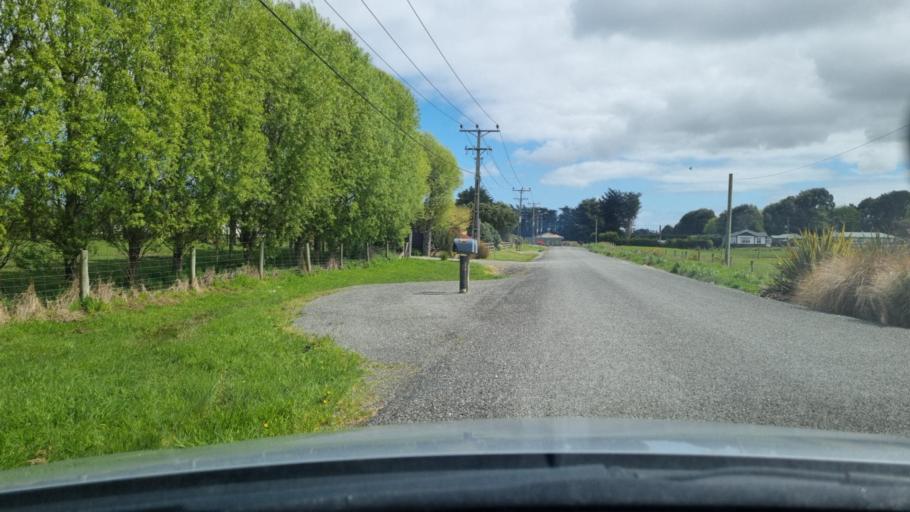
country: NZ
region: Southland
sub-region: Invercargill City
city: Invercargill
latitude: -46.4432
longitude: 168.3843
